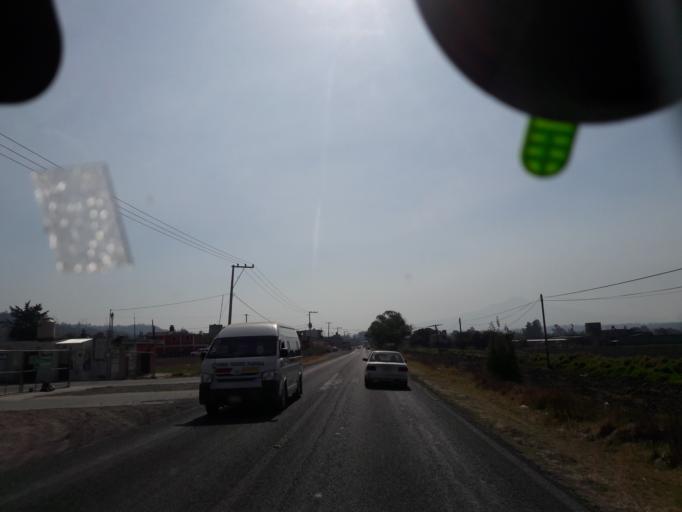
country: MX
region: Tlaxcala
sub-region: Panotla
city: Fraccionamiento la Virgen
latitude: 19.3208
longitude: -98.2910
